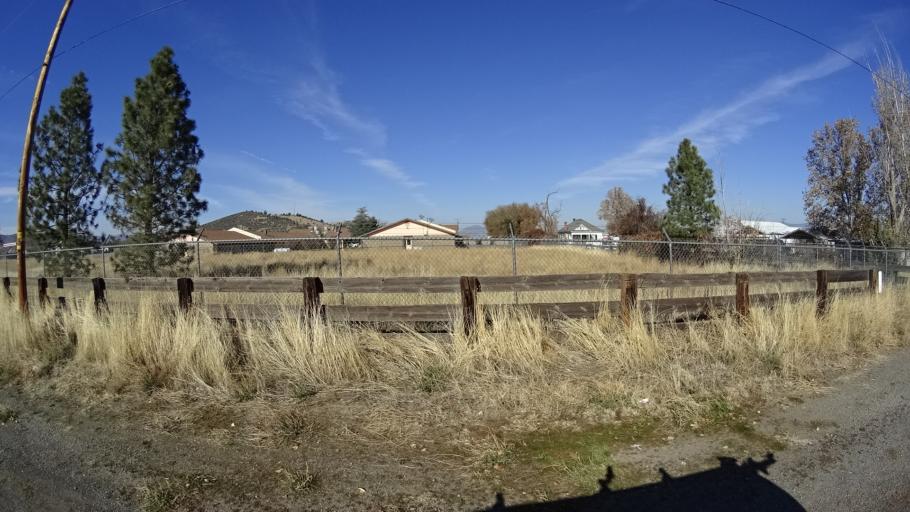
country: US
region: California
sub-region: Siskiyou County
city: Montague
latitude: 41.6456
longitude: -122.5263
